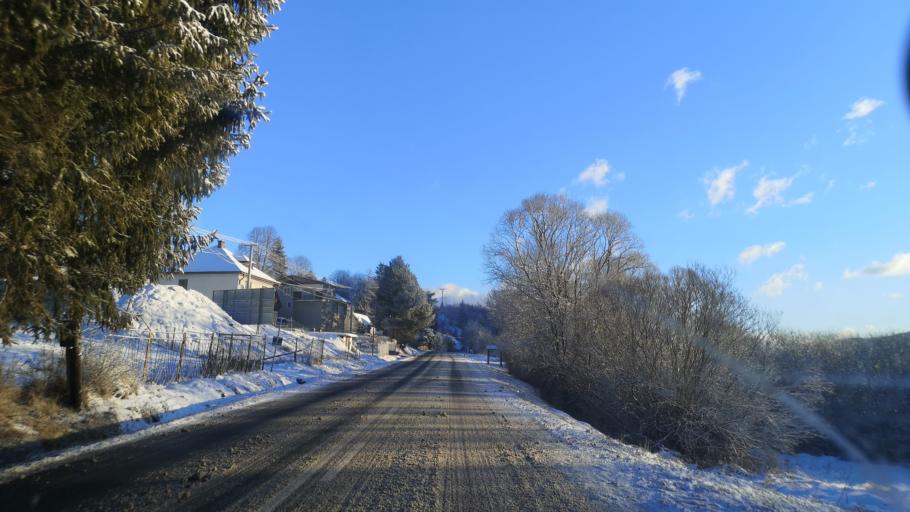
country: SK
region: Banskobystricky
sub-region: Okres Banska Bystrica
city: Brezno
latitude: 48.8229
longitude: 19.7226
